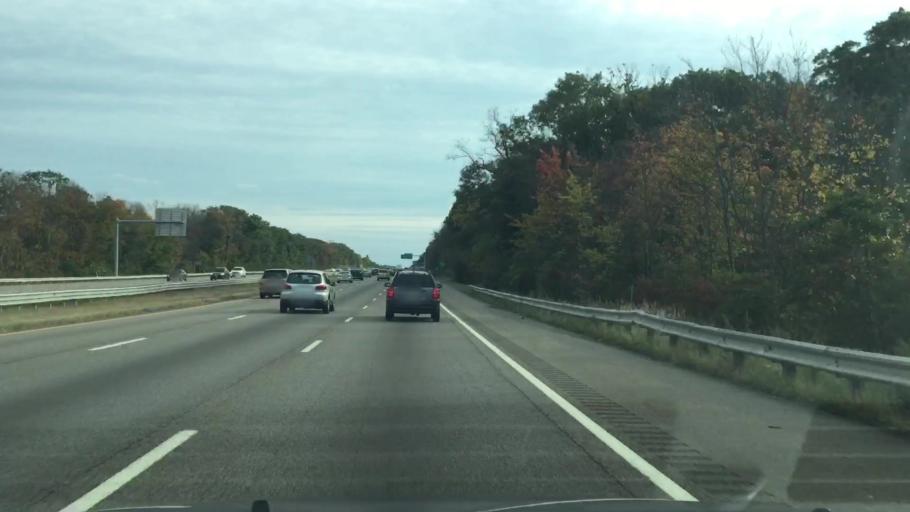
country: US
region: Massachusetts
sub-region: Norfolk County
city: Randolph
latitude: 42.1468
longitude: -71.0670
